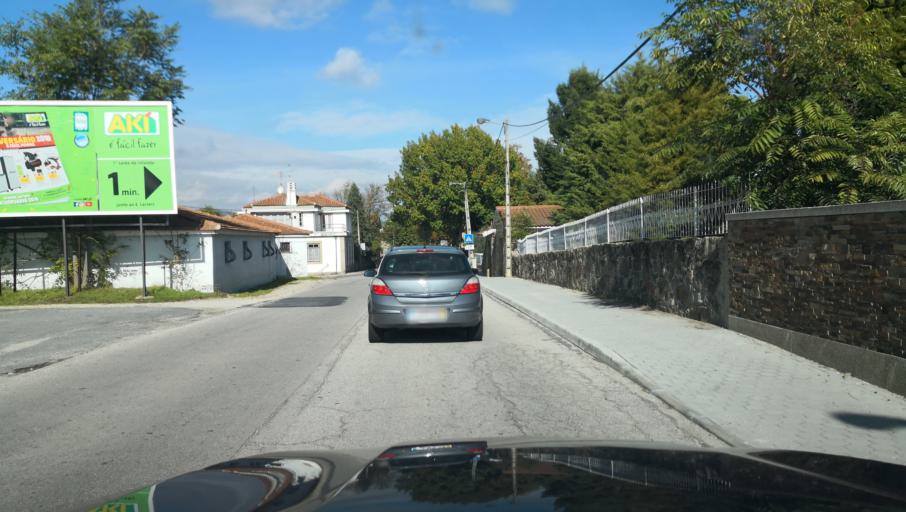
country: PT
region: Vila Real
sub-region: Chaves
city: Chaves
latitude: 41.7356
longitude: -7.4782
